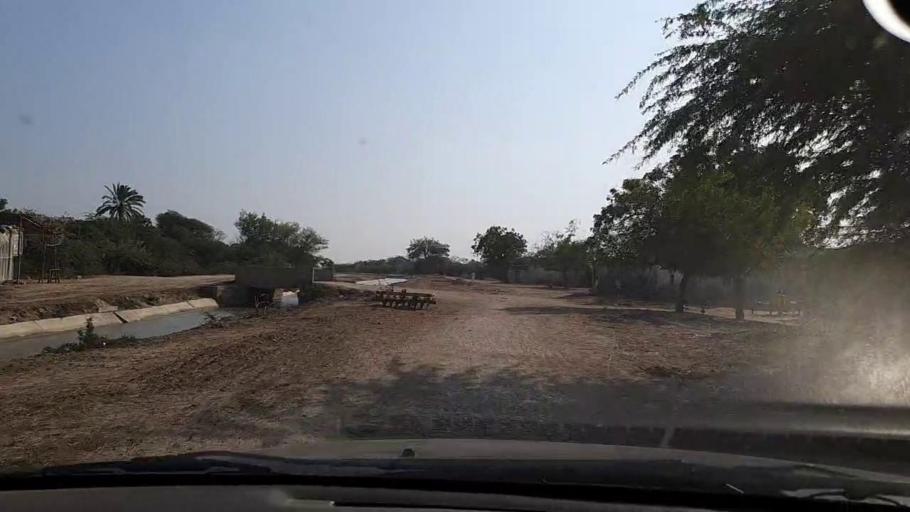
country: PK
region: Sindh
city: Mirpur Sakro
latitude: 24.3130
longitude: 67.7027
